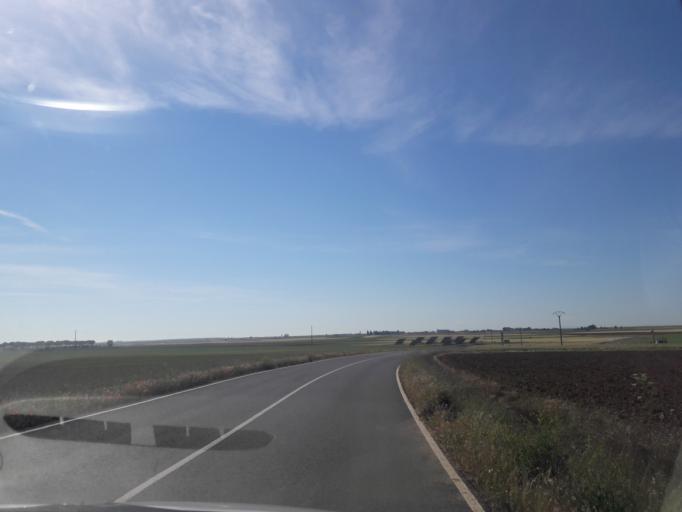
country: ES
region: Castille and Leon
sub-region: Provincia de Salamanca
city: Espino de la Orbada
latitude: 41.1026
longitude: -5.4198
